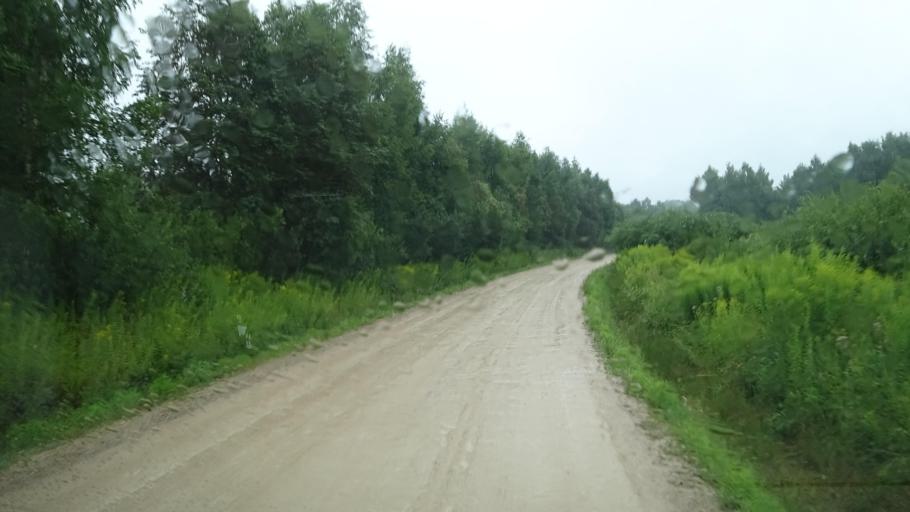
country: LV
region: Lecava
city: Iecava
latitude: 56.6636
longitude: 24.1671
